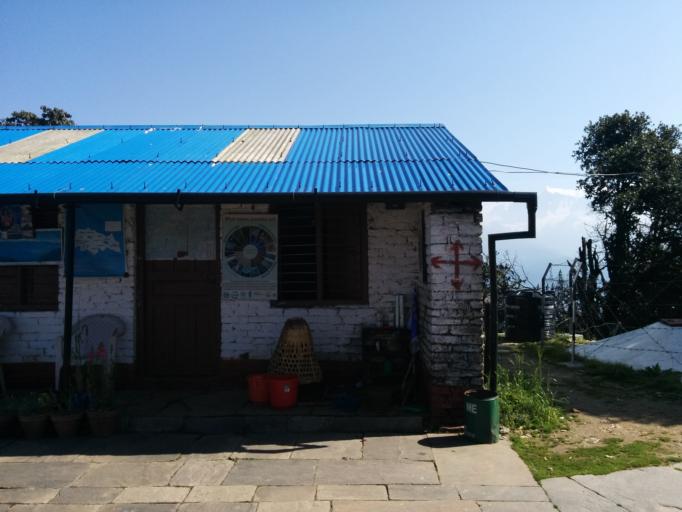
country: NP
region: Western Region
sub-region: Gandaki Zone
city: Pokhara
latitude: 28.2288
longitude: 83.7975
